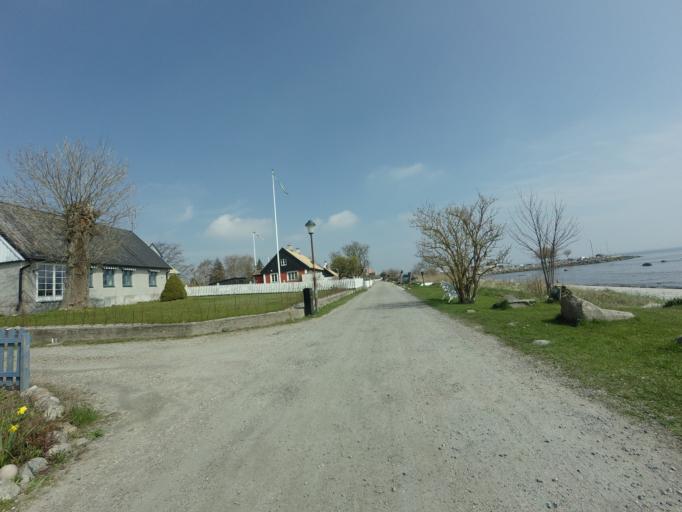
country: SE
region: Skane
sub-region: Skurups Kommun
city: Skivarp
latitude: 55.3928
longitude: 13.6000
